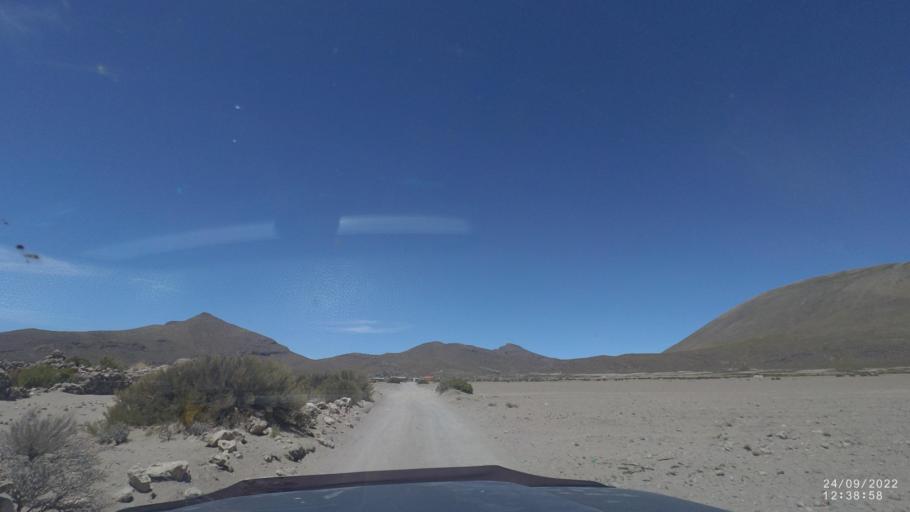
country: BO
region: Potosi
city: Colchani
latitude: -19.7921
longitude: -67.5815
